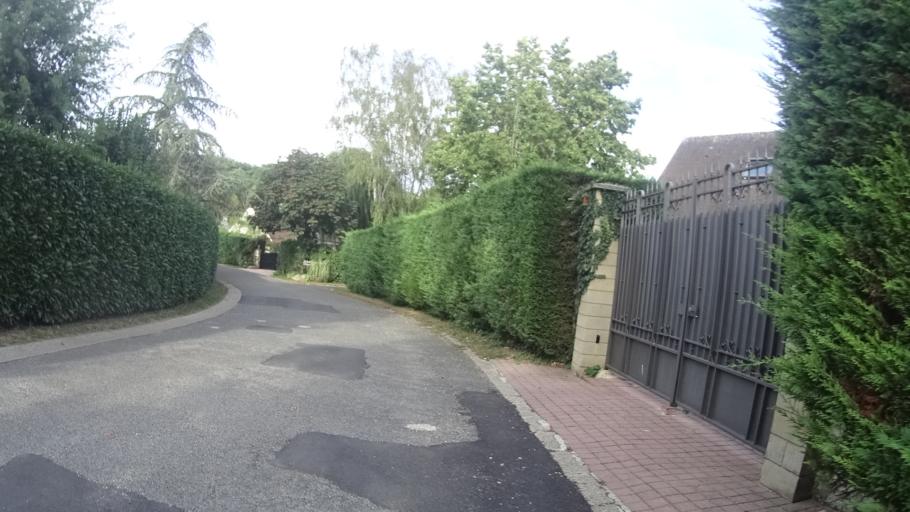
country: FR
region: Picardie
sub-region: Departement de l'Oise
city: Ver-sur-Launette
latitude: 49.1279
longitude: 2.7004
